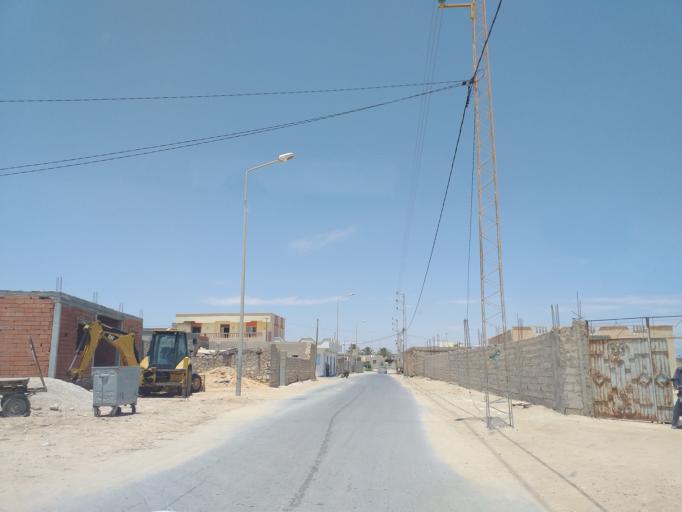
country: TN
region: Qabis
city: Gabes
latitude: 33.9443
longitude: 10.0592
